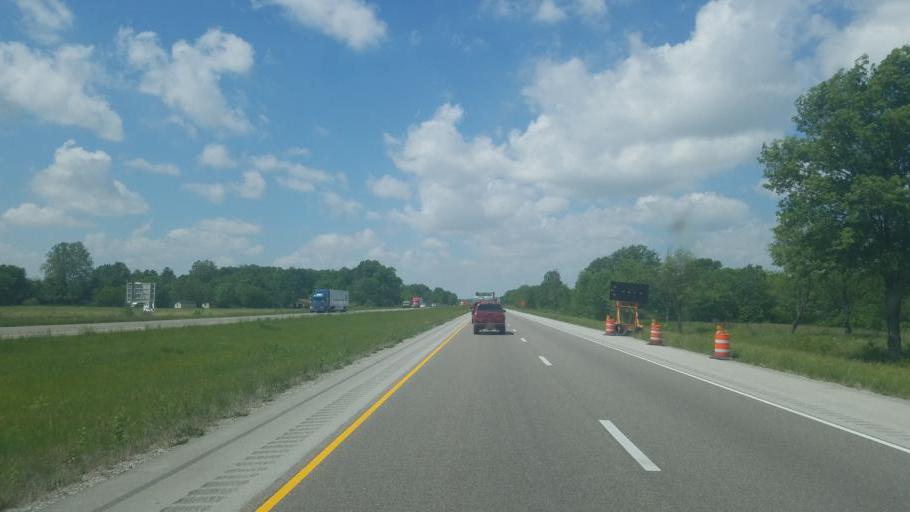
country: US
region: Illinois
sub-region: Cumberland County
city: Toledo
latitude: 39.2243
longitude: -88.2310
